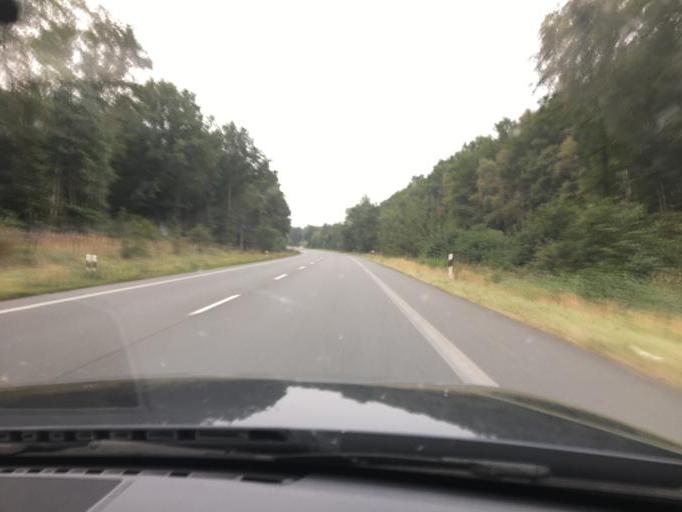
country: DE
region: North Rhine-Westphalia
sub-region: Regierungsbezirk Munster
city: Greven
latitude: 52.0523
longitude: 7.6801
